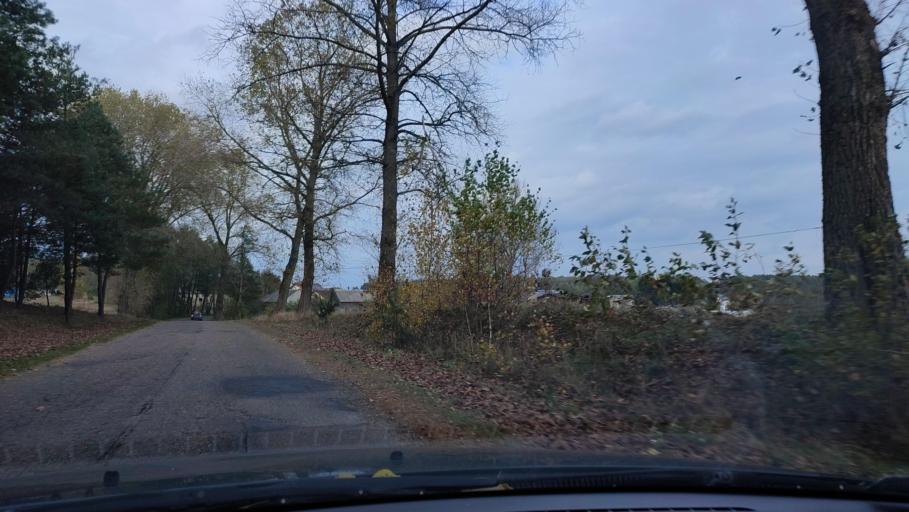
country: PL
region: Masovian Voivodeship
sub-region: Powiat mlawski
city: Mlawa
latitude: 53.1802
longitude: 20.3674
